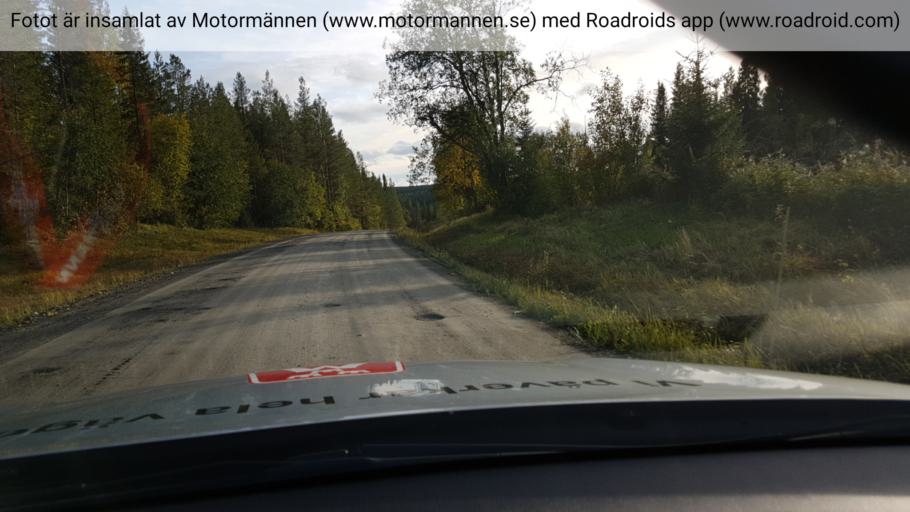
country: SE
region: Jaemtland
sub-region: Krokoms Kommun
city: Krokom
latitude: 63.6823
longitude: 14.5791
